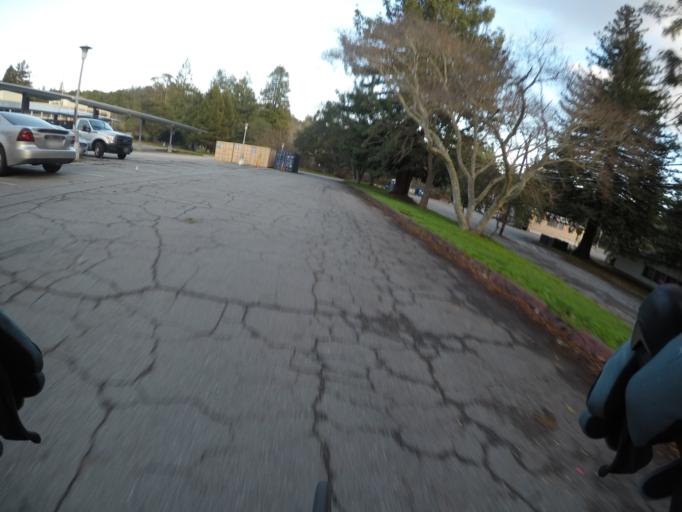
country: US
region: California
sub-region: Santa Cruz County
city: Pasatiempo
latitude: 36.9907
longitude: -122.0168
